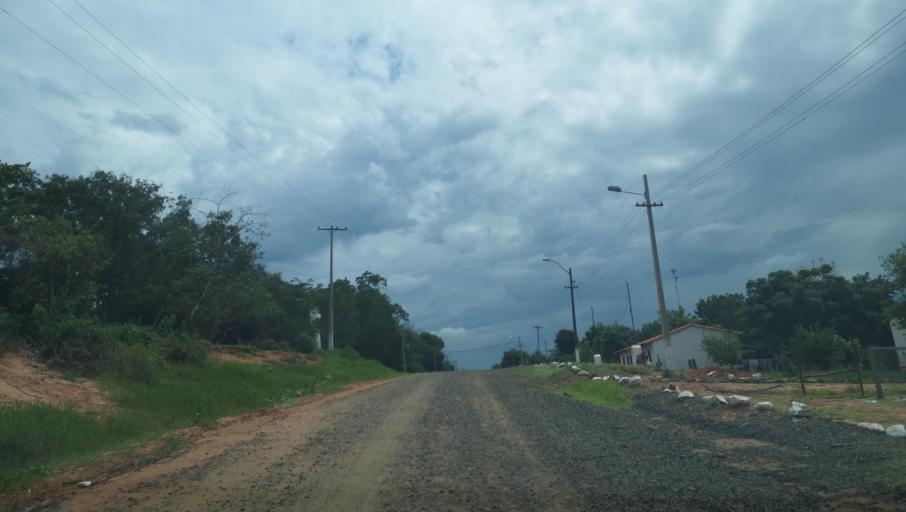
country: PY
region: San Pedro
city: Capiibary
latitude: -24.7267
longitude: -56.0086
